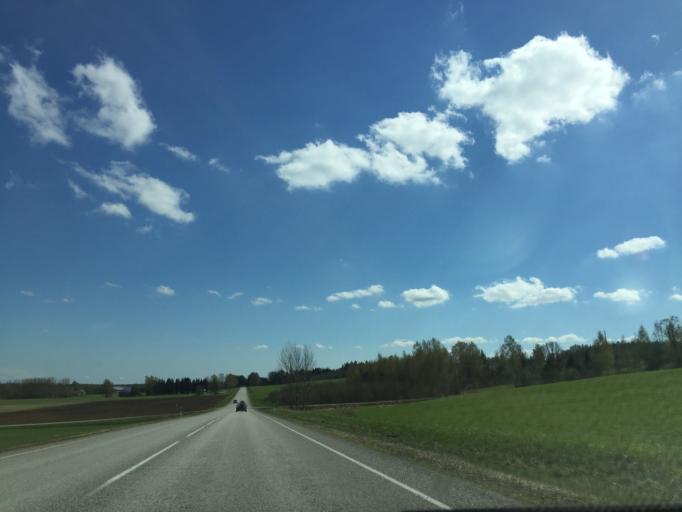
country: EE
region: Valgamaa
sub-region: Valga linn
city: Valga
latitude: 57.8994
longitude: 26.0508
